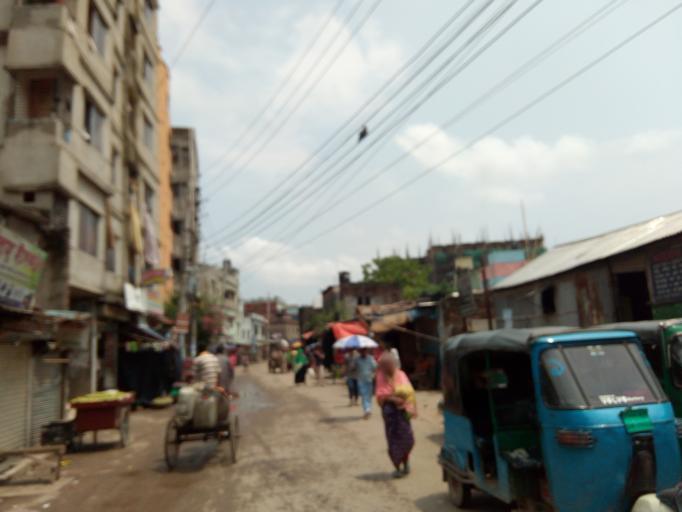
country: BD
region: Dhaka
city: Azimpur
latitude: 23.7456
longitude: 90.3633
